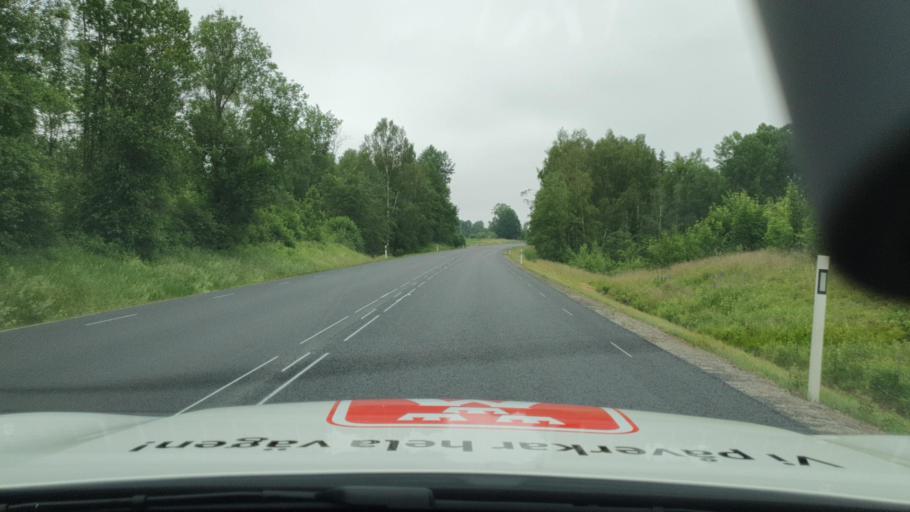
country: SE
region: Vaermland
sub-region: Sunne Kommun
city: Sunne
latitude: 59.8570
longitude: 13.1268
